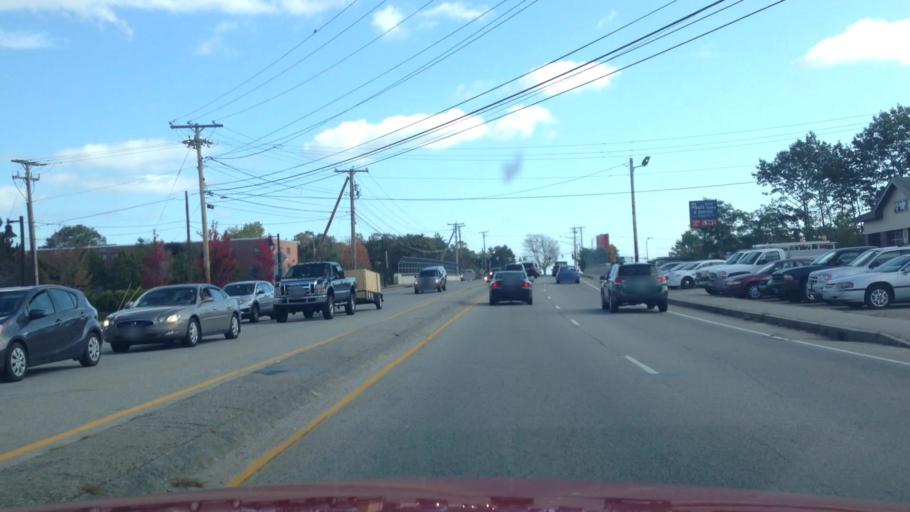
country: US
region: Maine
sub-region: Cumberland County
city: South Portland Gardens
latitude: 43.6768
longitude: -70.3286
